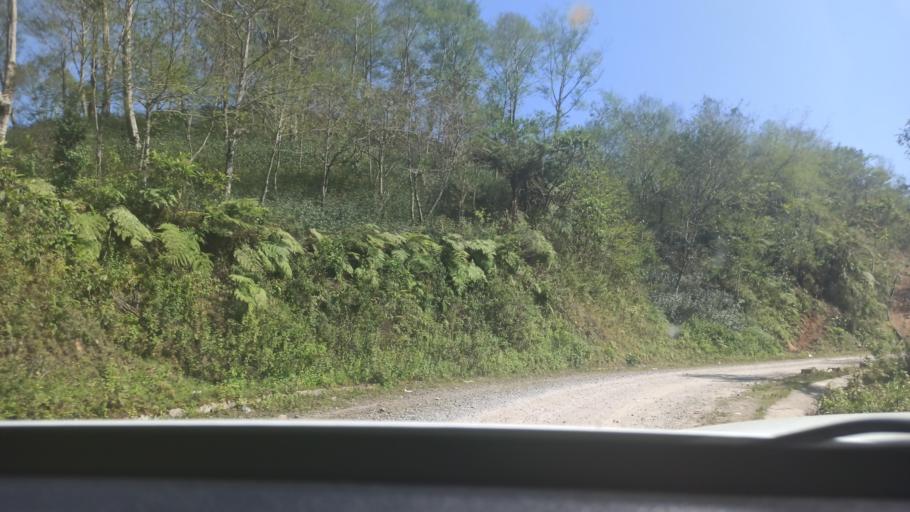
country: MX
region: Veracruz
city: Xocotla
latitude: 18.9699
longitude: -97.0894
